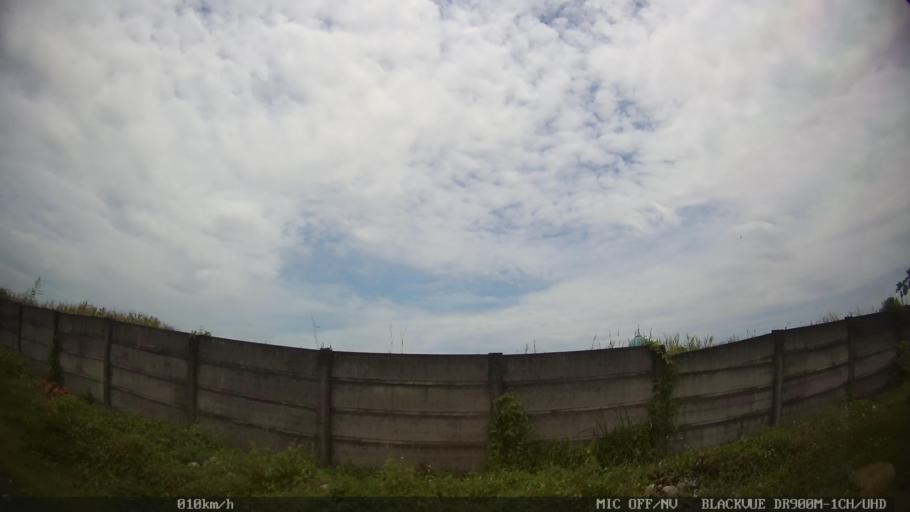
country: ID
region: North Sumatra
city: Sunggal
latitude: 3.6217
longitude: 98.5807
